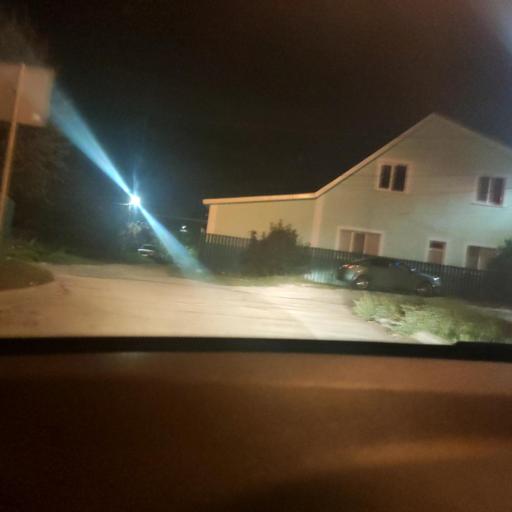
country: RU
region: Samara
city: Samara
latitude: 53.2218
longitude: 50.2178
